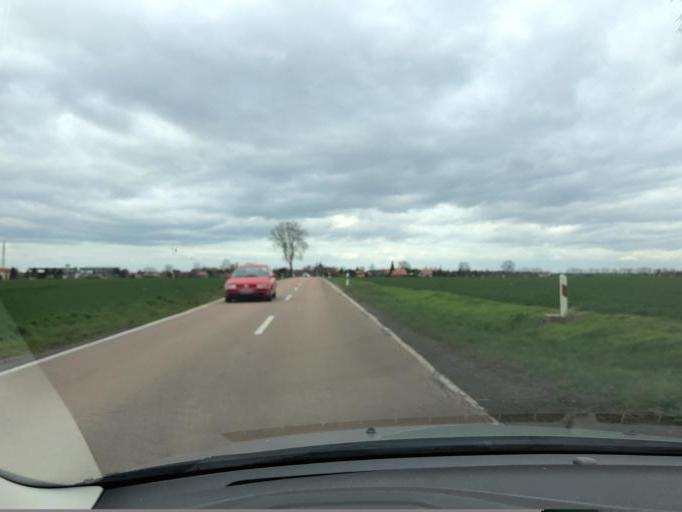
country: DE
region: Saxony-Anhalt
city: Muschwitz
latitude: 51.2096
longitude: 12.1392
